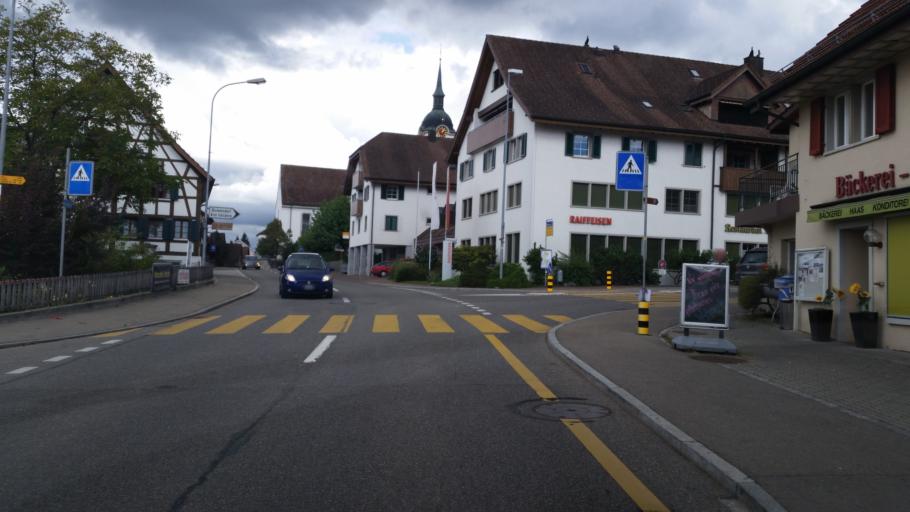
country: CH
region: Aargau
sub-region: Bezirk Bremgarten
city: Oberlunkhofen
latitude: 47.3111
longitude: 8.3902
